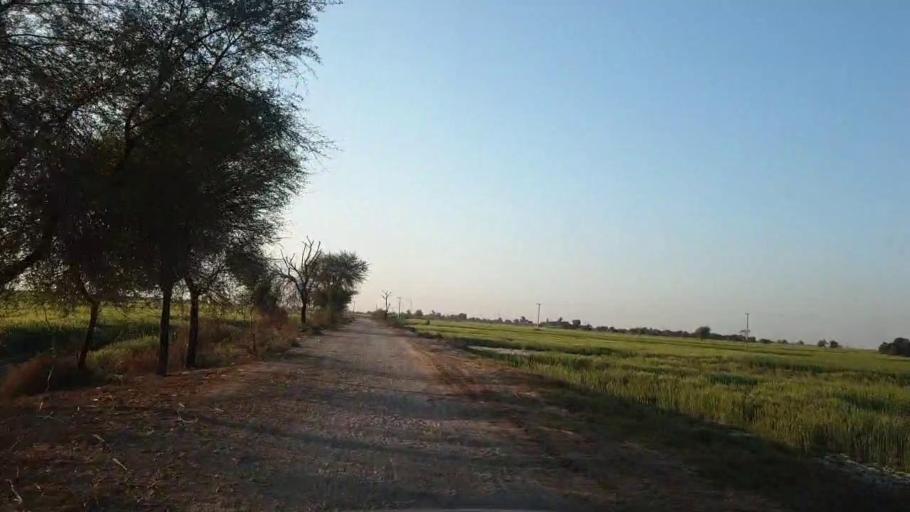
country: PK
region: Sindh
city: Mirpur Khas
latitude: 25.6955
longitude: 69.0494
